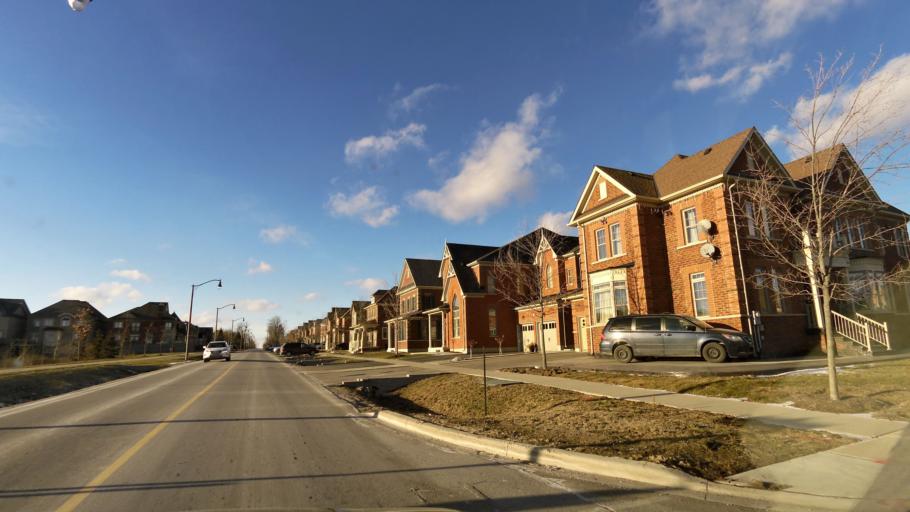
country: CA
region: Ontario
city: Brampton
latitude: 43.6591
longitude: -79.7955
